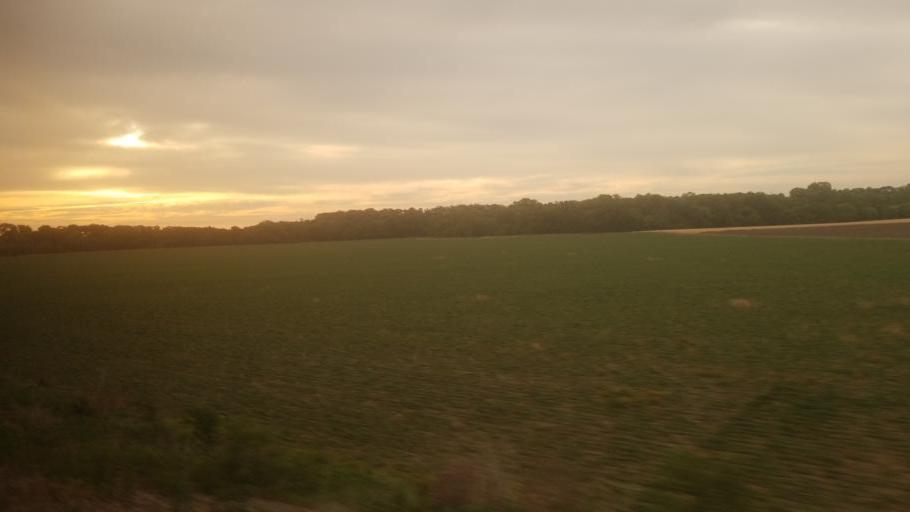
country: US
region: Kansas
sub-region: Chase County
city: Cottonwood Falls
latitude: 38.3828
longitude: -96.6379
